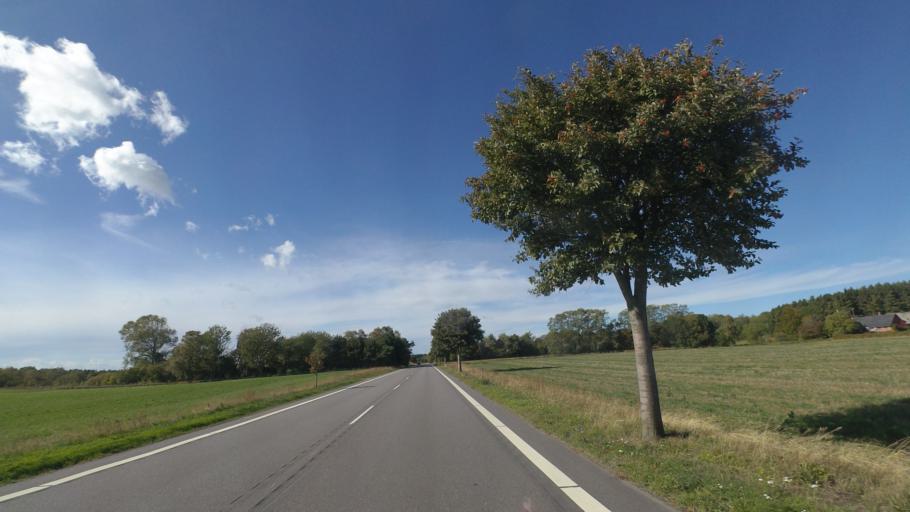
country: DK
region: Capital Region
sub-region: Bornholm Kommune
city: Ronne
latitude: 55.0762
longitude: 14.7744
